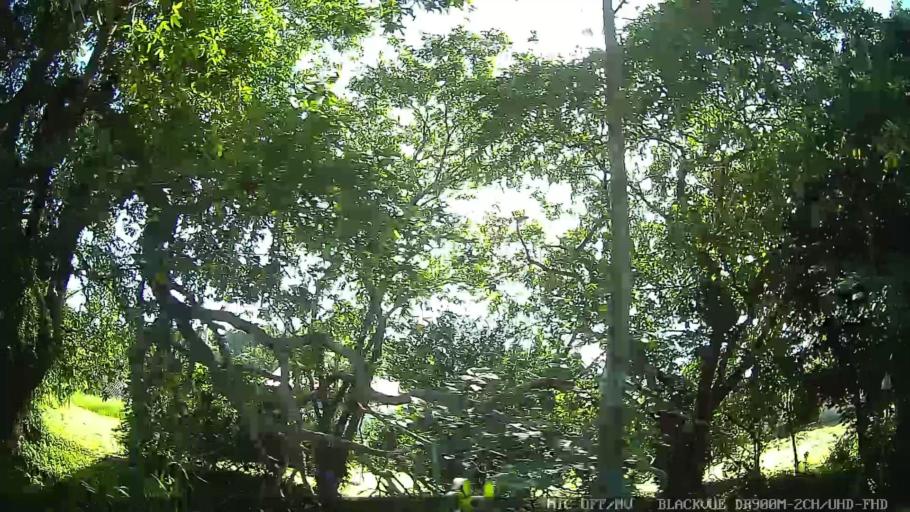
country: BR
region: Sao Paulo
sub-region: Peruibe
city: Peruibe
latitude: -24.2731
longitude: -46.9433
